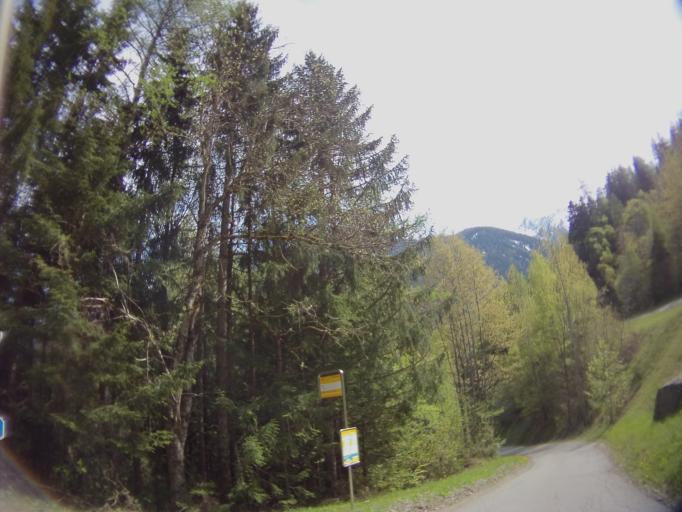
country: CH
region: Valais
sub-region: Martigny District
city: Martigny-Combe
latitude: 46.0764
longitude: 7.0287
